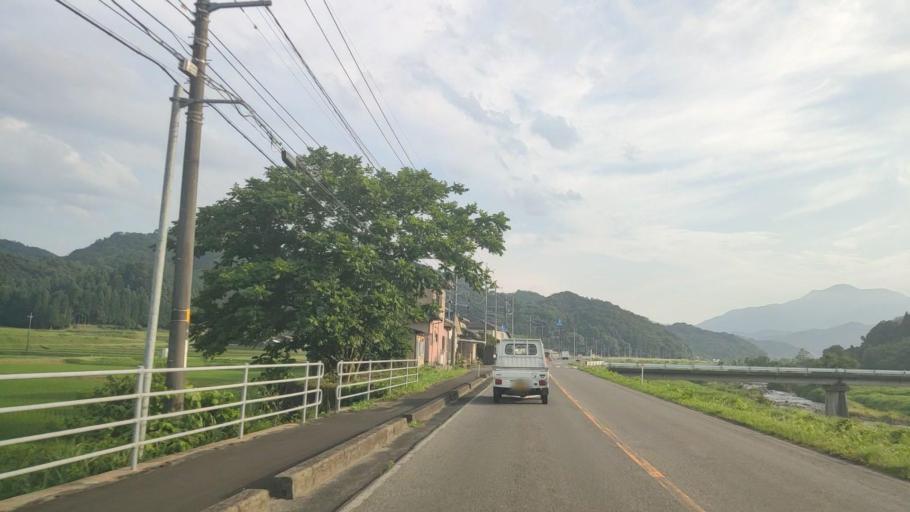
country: JP
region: Tottori
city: Kurayoshi
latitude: 35.3784
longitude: 133.7749
